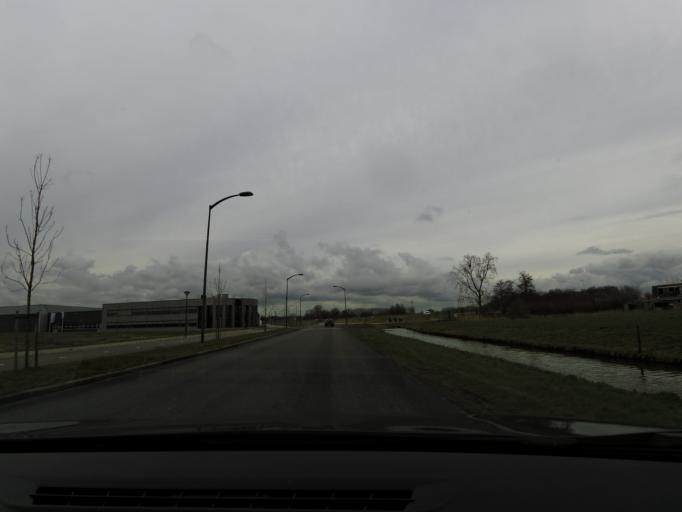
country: NL
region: South Holland
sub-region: Gemeente Waddinxveen
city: Waddinxveen
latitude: 52.0161
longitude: 4.6618
